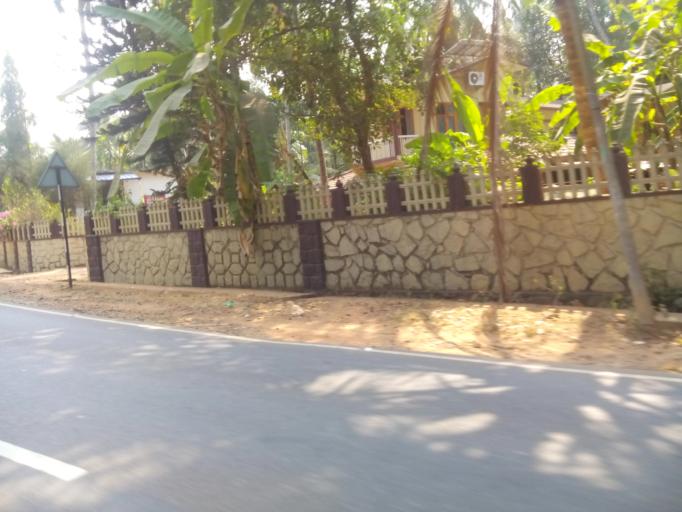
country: IN
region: Kerala
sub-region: Kozhikode
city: Naduvannur
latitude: 11.5726
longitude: 75.7537
